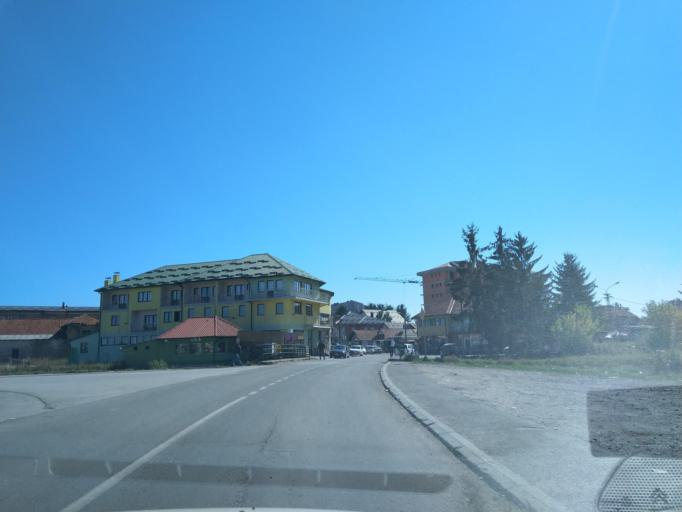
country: RS
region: Central Serbia
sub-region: Zlatiborski Okrug
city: Sjenica
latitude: 43.2753
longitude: 20.0025
